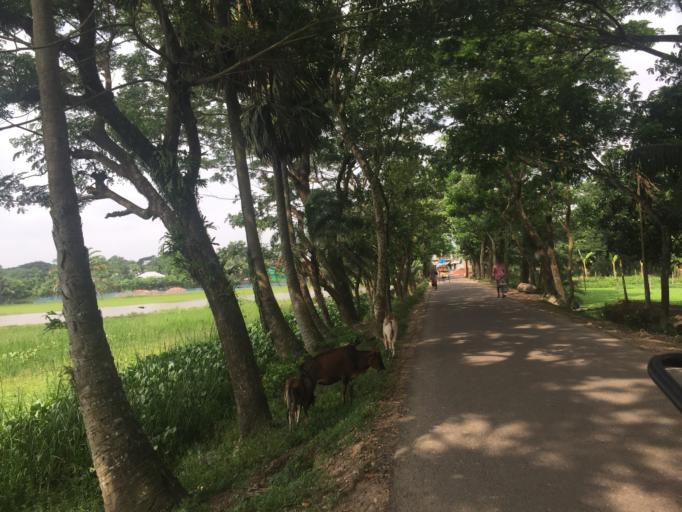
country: BD
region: Barisal
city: Mathba
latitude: 22.2147
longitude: 89.9143
